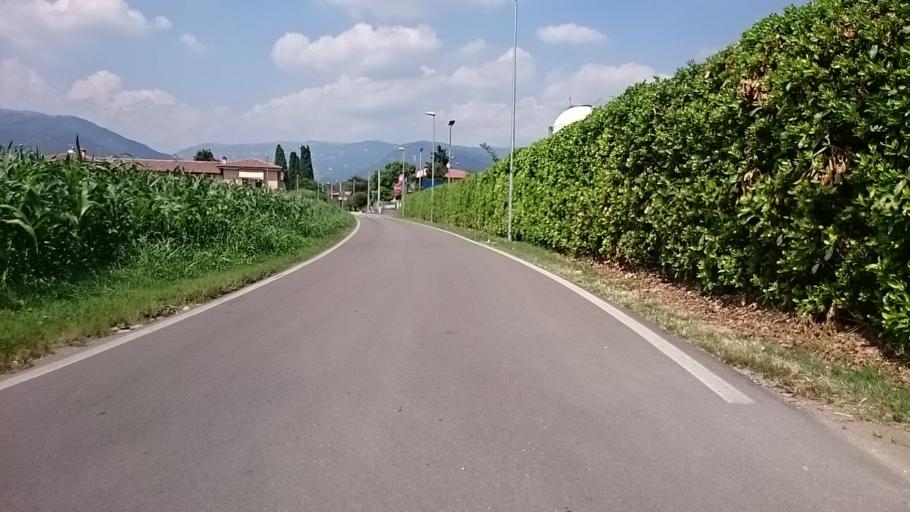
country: IT
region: Veneto
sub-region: Provincia di Vicenza
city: Bassano del Grappa
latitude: 45.7471
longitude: 11.7304
